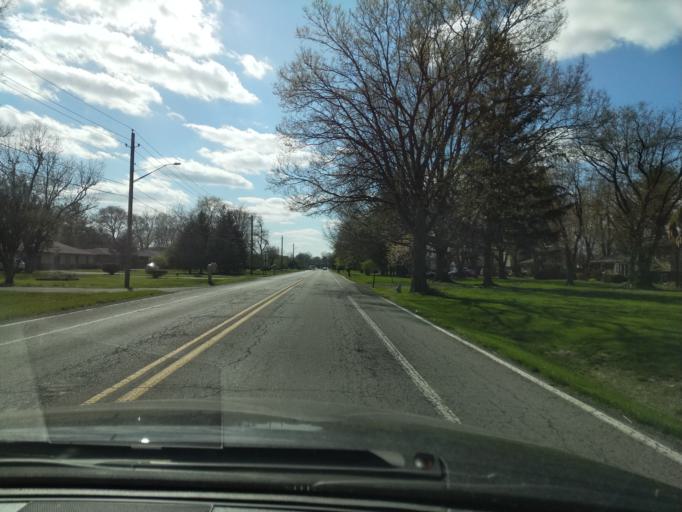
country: US
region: Indiana
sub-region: Marion County
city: Meridian Hills
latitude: 39.8865
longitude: -86.1779
